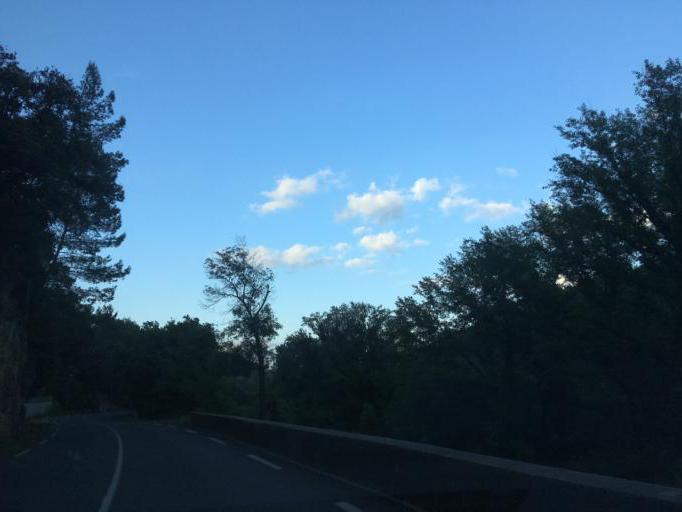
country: FR
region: Provence-Alpes-Cote d'Azur
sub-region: Departement du Var
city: Carces
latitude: 43.4791
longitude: 6.1971
